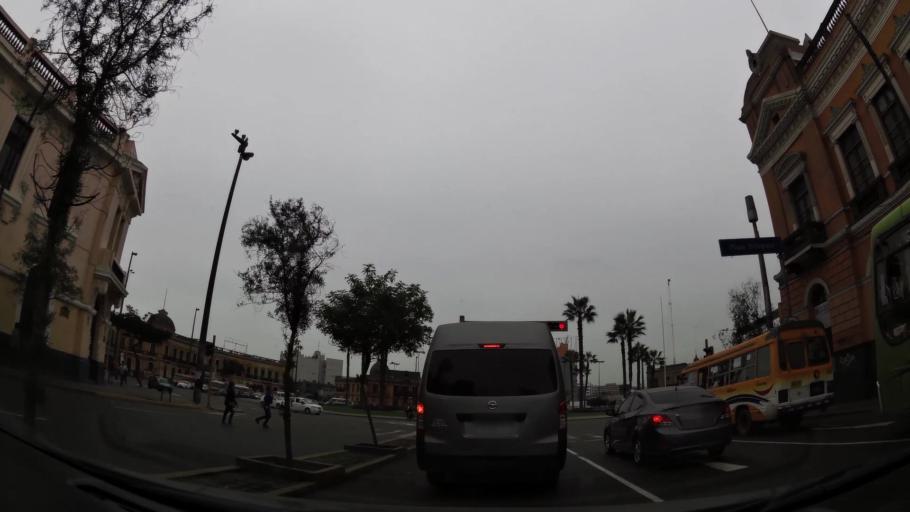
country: PE
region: Lima
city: Lima
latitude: -12.0610
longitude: -77.0412
